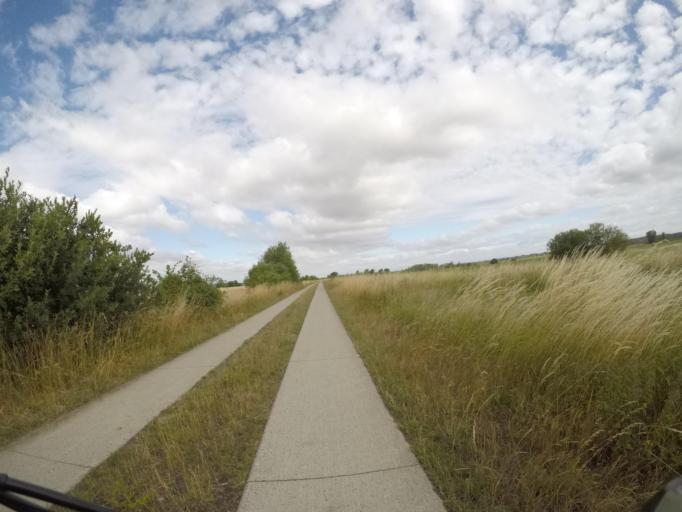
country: DE
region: Lower Saxony
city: Hitzacker
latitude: 53.1738
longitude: 11.0502
